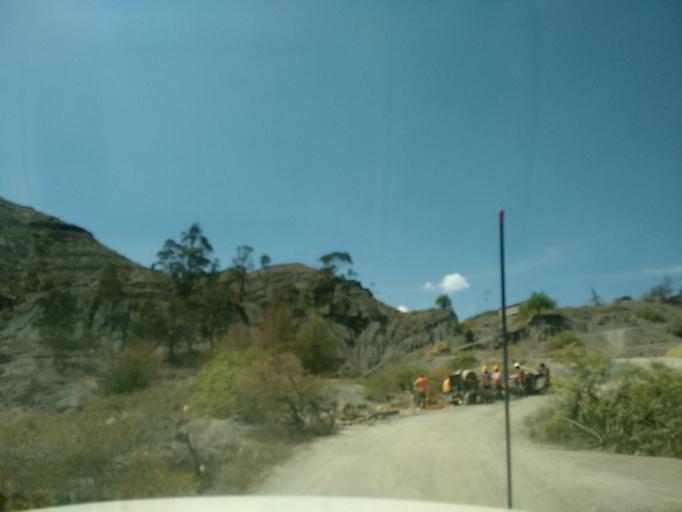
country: CO
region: Boyaca
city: Sachica
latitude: 5.5890
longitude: -73.5159
